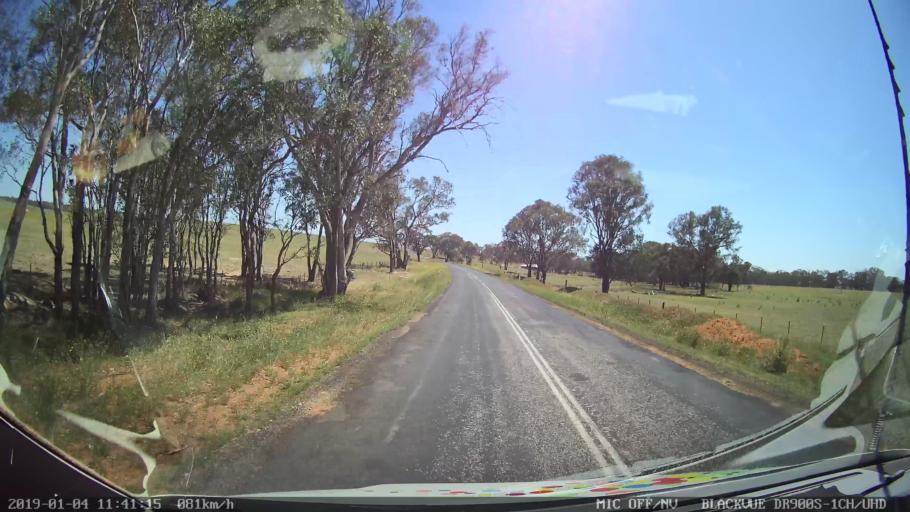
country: AU
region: New South Wales
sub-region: Cabonne
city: Molong
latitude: -32.9959
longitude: 148.7872
